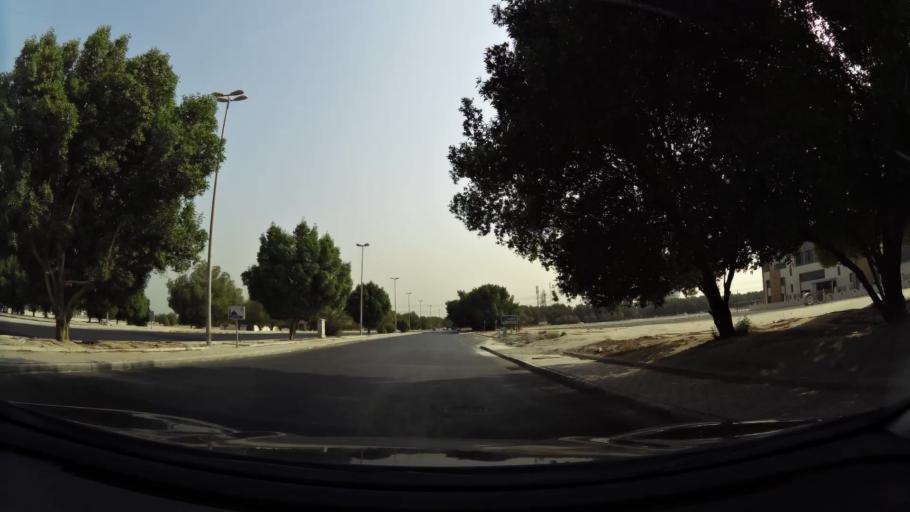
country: KW
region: Mubarak al Kabir
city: Sabah as Salim
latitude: 29.2716
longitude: 48.0557
